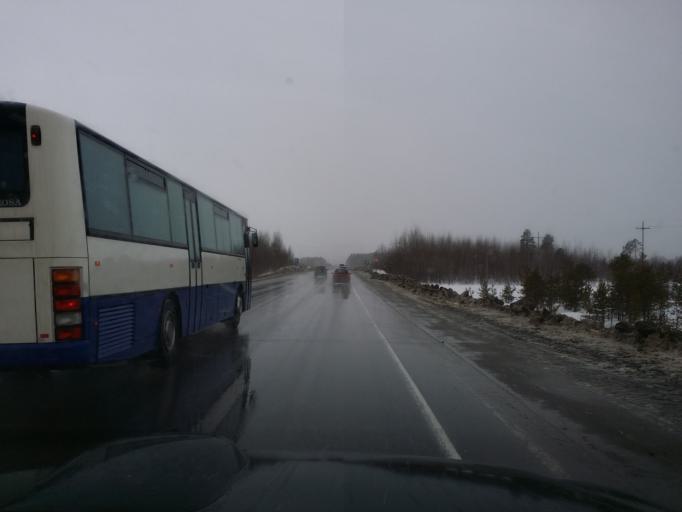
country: RU
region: Khanty-Mansiyskiy Avtonomnyy Okrug
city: Nizhnevartovsk
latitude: 60.9556
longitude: 76.7137
